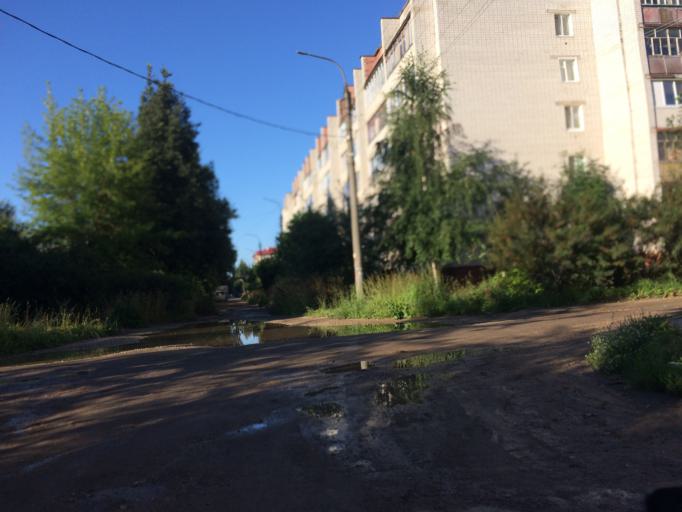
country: RU
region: Mariy-El
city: Yoshkar-Ola
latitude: 56.6489
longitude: 47.8893
